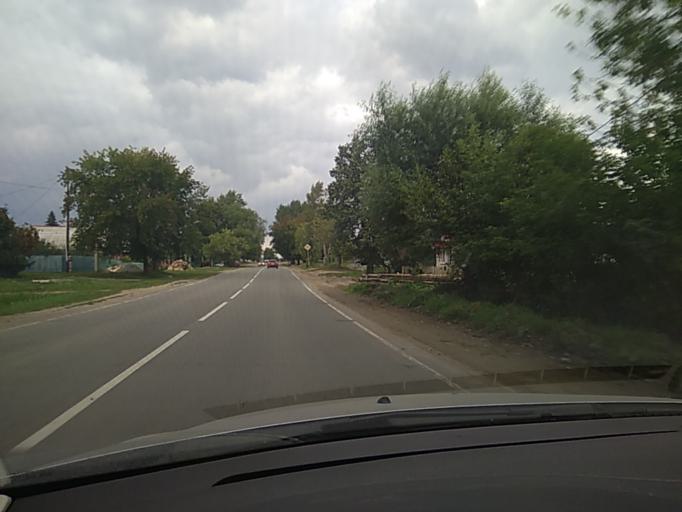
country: RU
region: Chelyabinsk
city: Kyshtym
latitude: 55.7066
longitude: 60.5187
